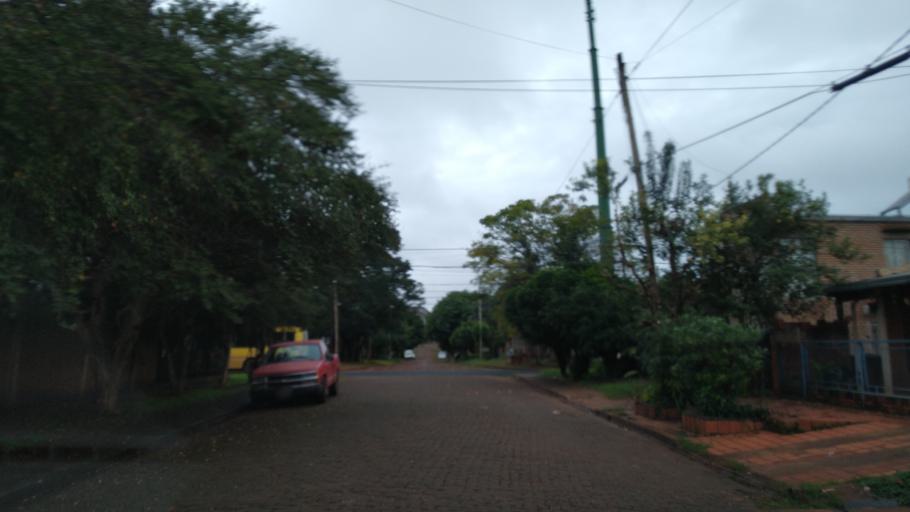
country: AR
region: Misiones
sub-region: Departamento de Capital
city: Posadas
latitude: -27.4000
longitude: -55.9349
